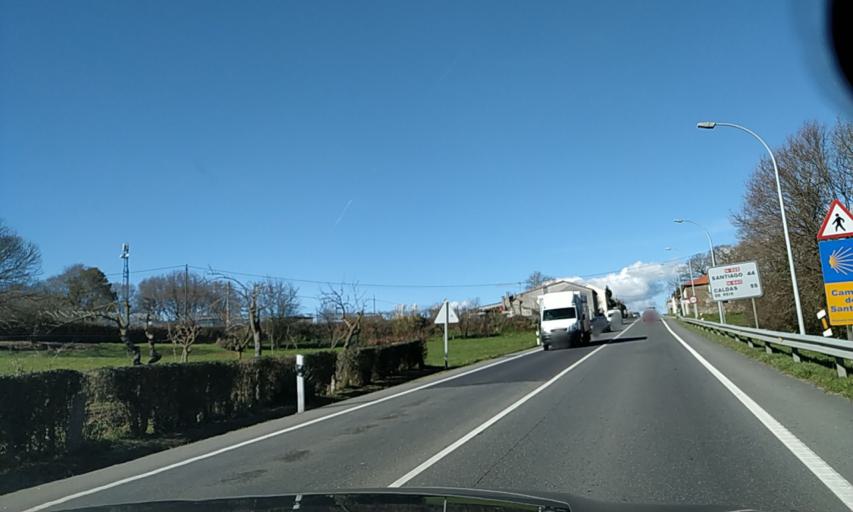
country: ES
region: Galicia
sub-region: Provincia de Pontevedra
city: Lalin
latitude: 42.6762
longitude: -8.1648
